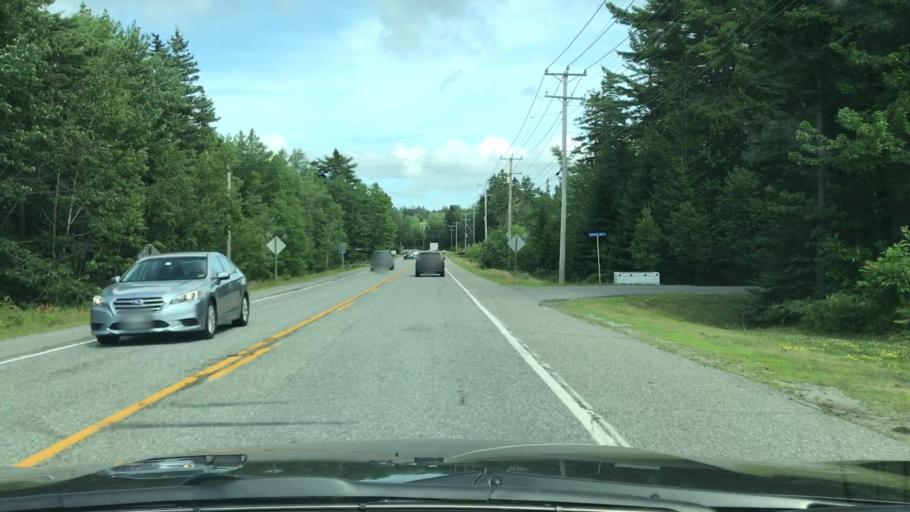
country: US
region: Maine
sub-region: Hancock County
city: Trenton
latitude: 44.4197
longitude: -68.3565
